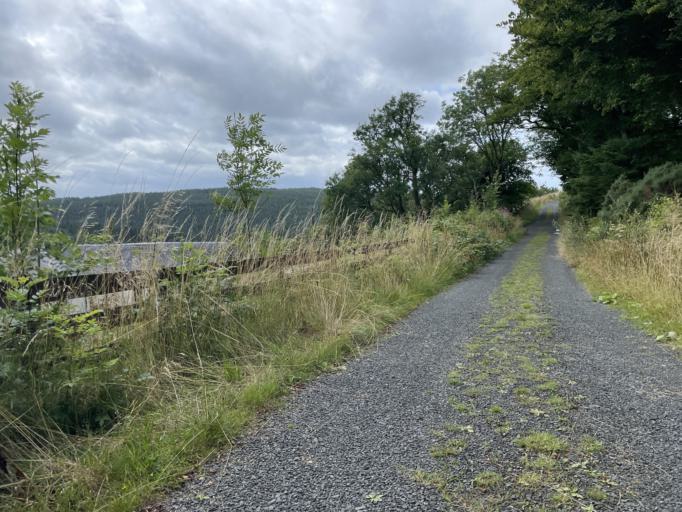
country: GB
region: Scotland
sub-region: South Ayrshire
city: Maybole
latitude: 55.2072
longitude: -4.6744
